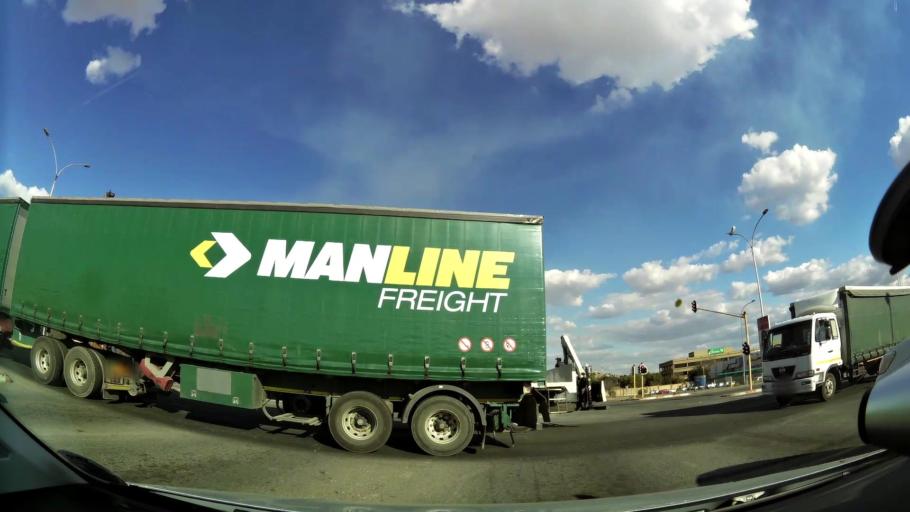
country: ZA
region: North-West
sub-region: Dr Kenneth Kaunda District Municipality
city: Klerksdorp
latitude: -26.8558
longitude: 26.6776
